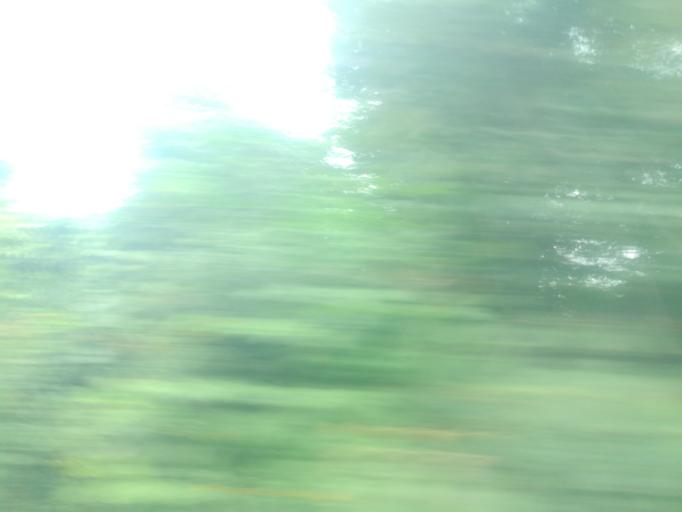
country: NG
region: Ogun
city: Ayetoro
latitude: 7.1035
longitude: 3.1480
